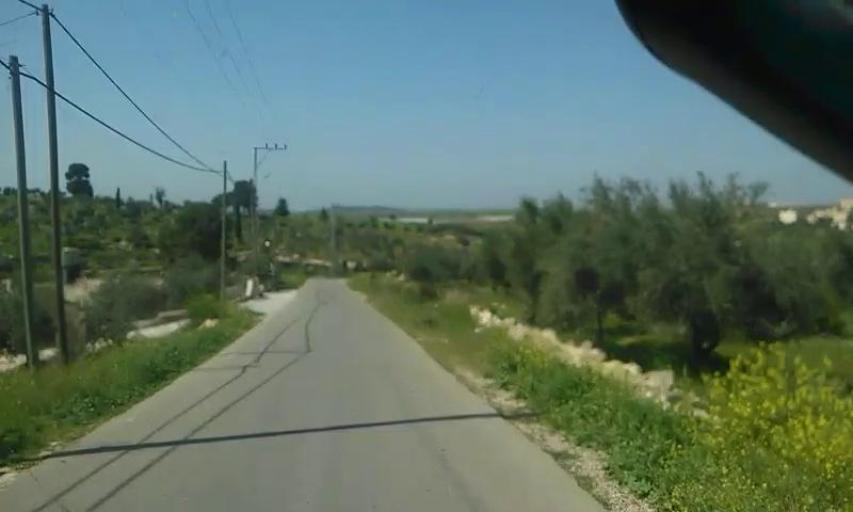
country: PS
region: West Bank
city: Al Majd
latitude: 31.4867
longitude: 34.9440
